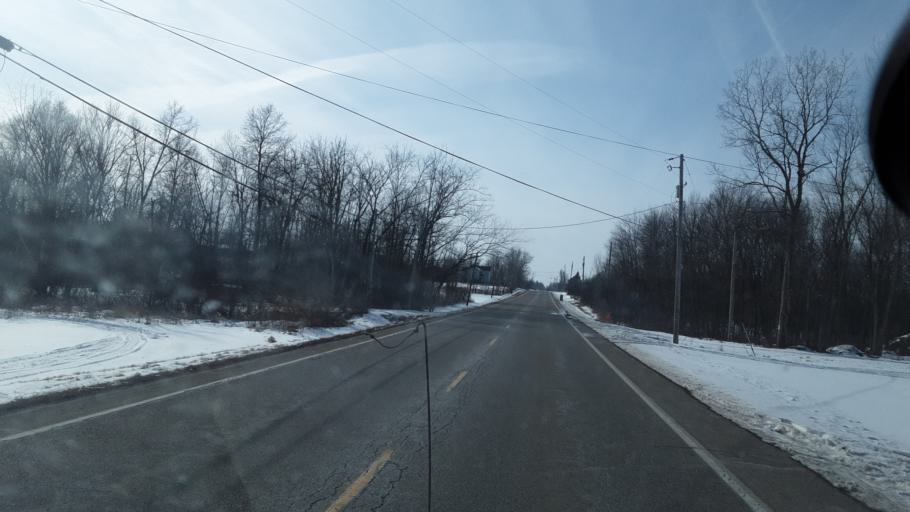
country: US
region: Ohio
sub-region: Mahoning County
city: Craig Beach
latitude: 41.0247
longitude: -81.0226
